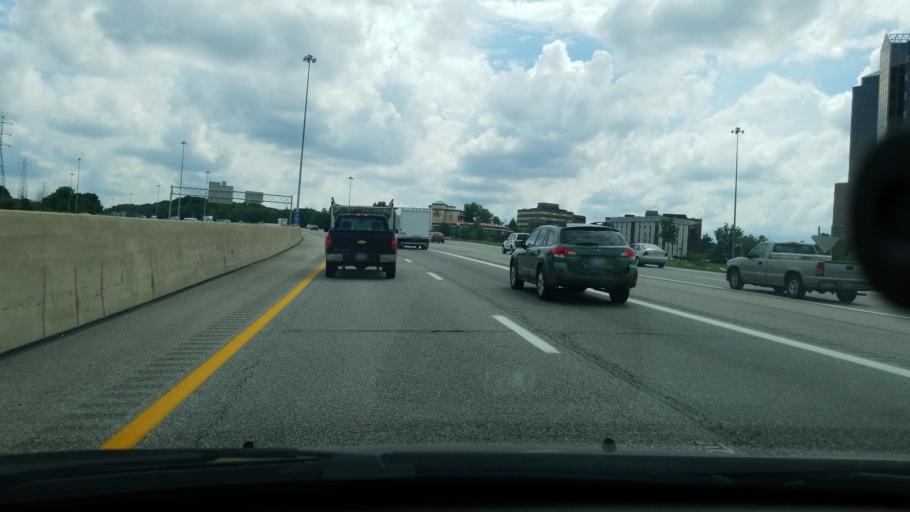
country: US
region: Ohio
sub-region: Cuyahoga County
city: Seven Hills
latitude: 41.3990
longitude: -81.6518
